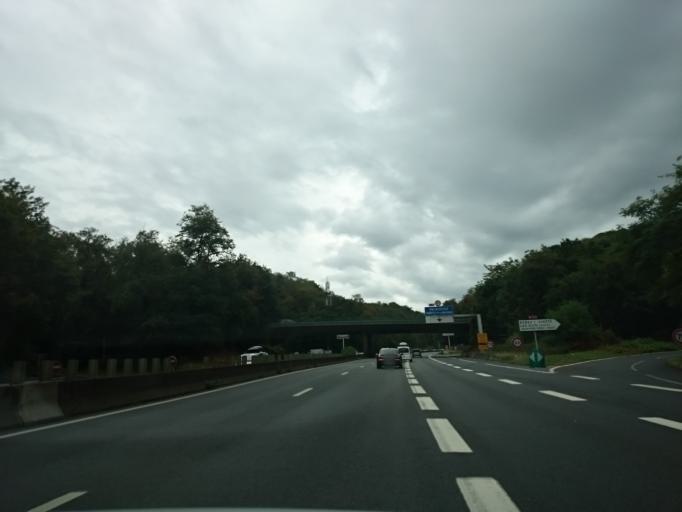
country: FR
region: Ile-de-France
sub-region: Departement de l'Essonne
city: Orsay
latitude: 48.6948
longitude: 2.1924
